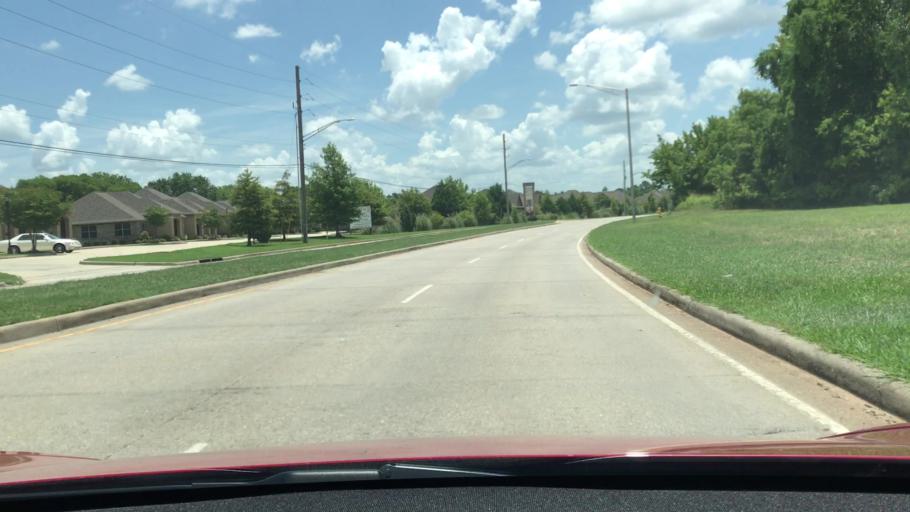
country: US
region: Louisiana
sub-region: Bossier Parish
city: Bossier City
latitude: 32.4344
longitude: -93.7270
